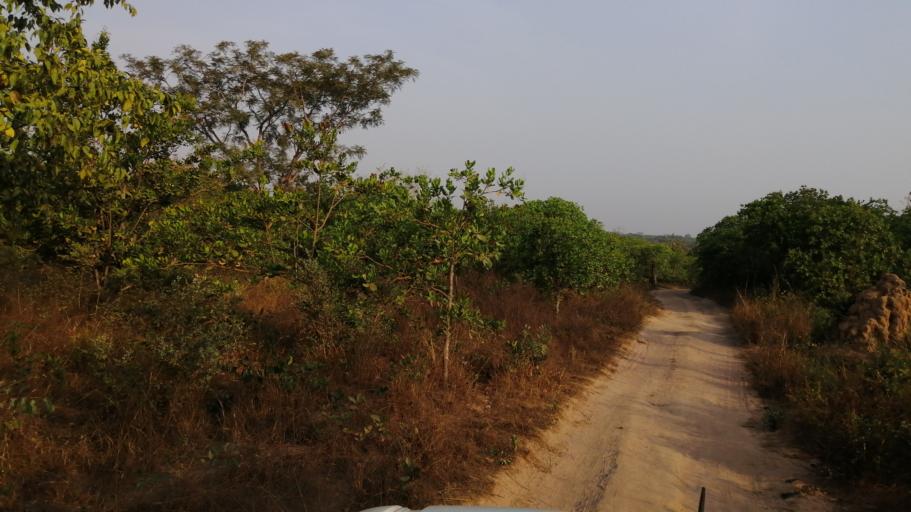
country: GW
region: Bissau
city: Bissau
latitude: 11.9823
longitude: -15.4688
